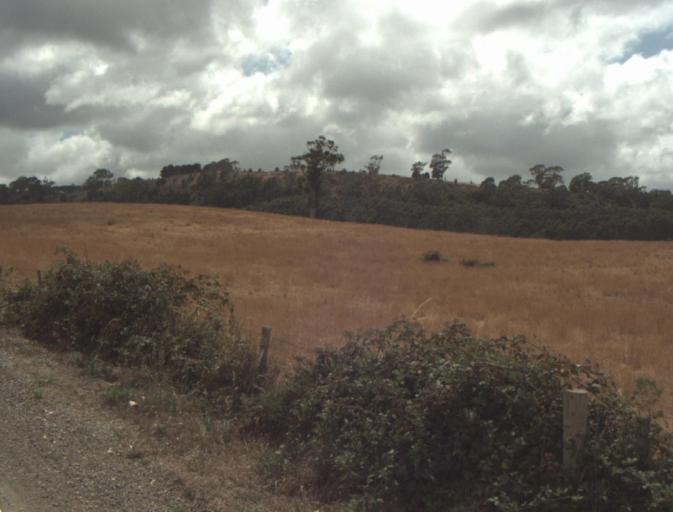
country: AU
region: Tasmania
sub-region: Launceston
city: Mayfield
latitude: -41.1752
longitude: 147.2148
